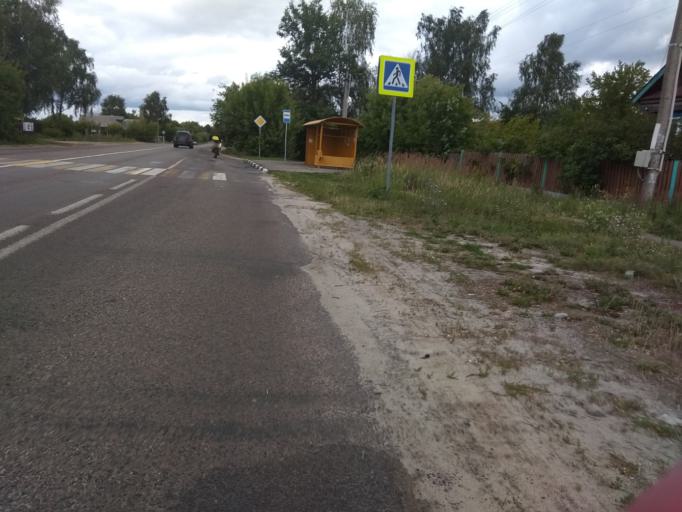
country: RU
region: Moskovskaya
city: Misheronskiy
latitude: 55.5984
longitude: 39.7046
